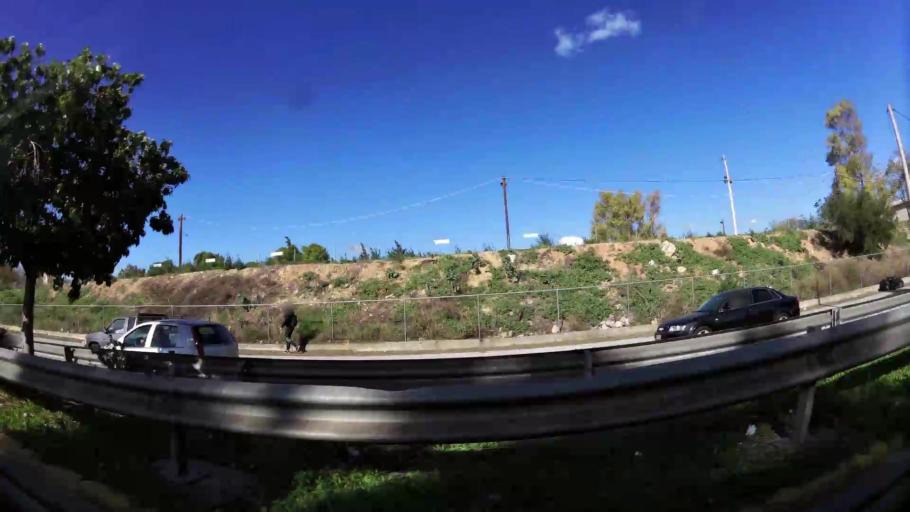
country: GR
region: Attica
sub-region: Nomarchia Athinas
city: Aigaleo
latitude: 37.9789
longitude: 23.6698
